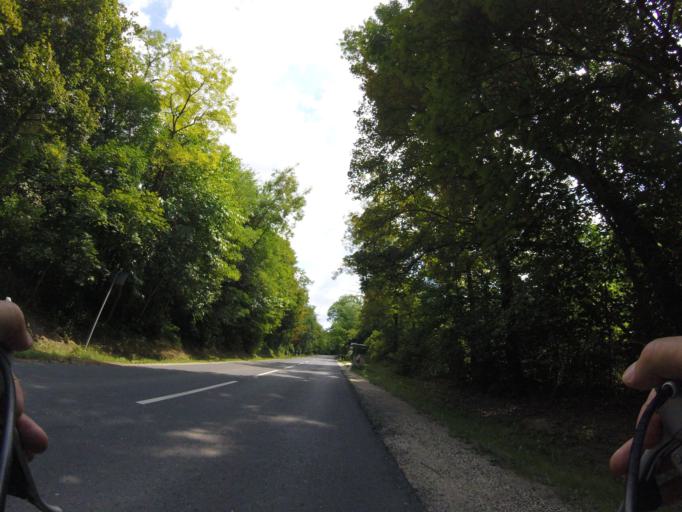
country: HU
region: Pest
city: Soskut
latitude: 47.4375
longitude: 18.8200
